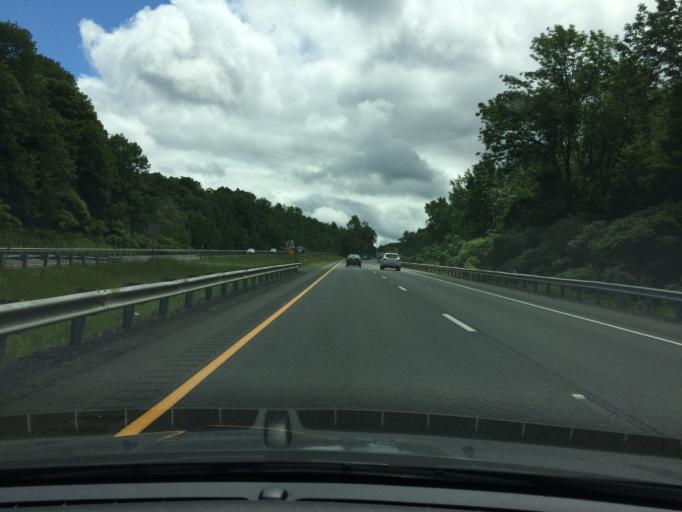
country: US
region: Massachusetts
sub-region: Berkshire County
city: Otis
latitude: 42.2574
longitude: -73.1233
